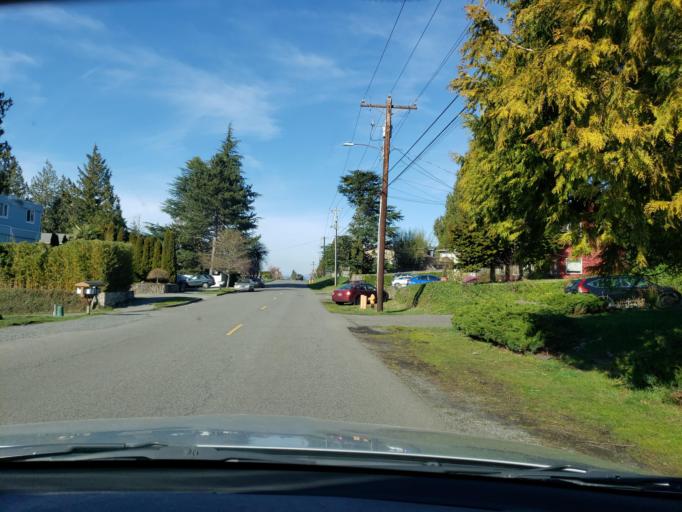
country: US
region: Washington
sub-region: Snohomish County
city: Woodway
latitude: 47.7976
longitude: -122.3695
